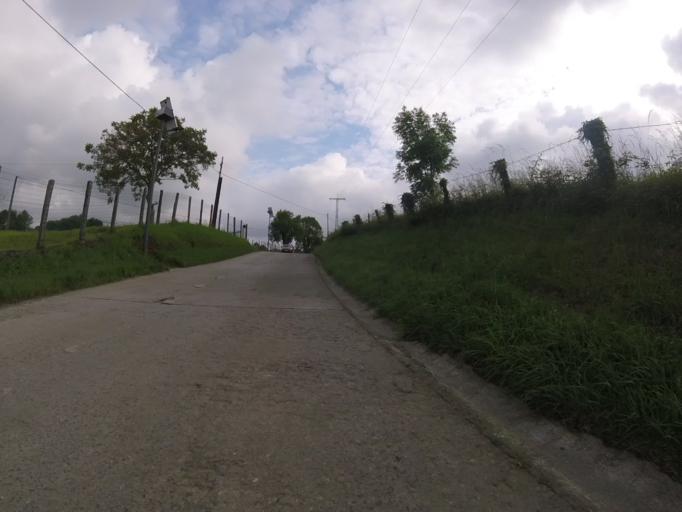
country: ES
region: Basque Country
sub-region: Provincia de Guipuzcoa
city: Astigarraga
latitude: 43.3013
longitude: -1.9330
